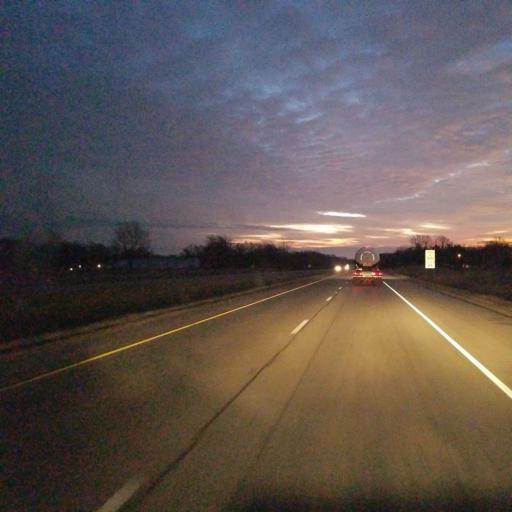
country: US
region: Illinois
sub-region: Peoria County
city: Bellevue
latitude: 40.6939
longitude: -89.6934
